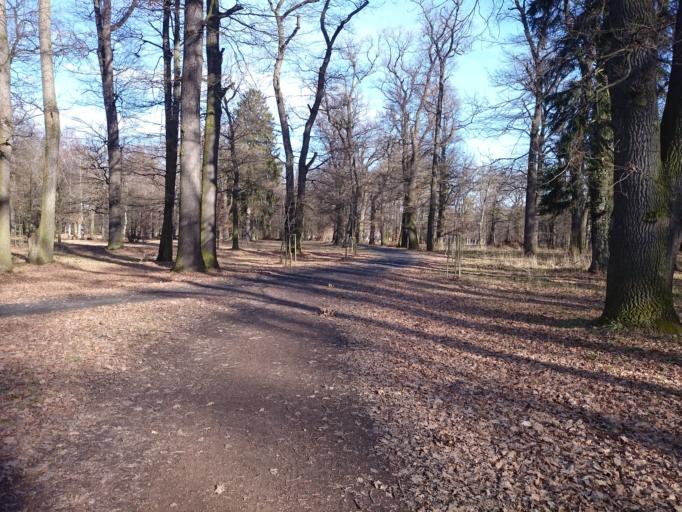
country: CZ
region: Pardubicky
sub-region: Okres Chrudim
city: Hermanuv Mestec
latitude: 49.9475
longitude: 15.6774
